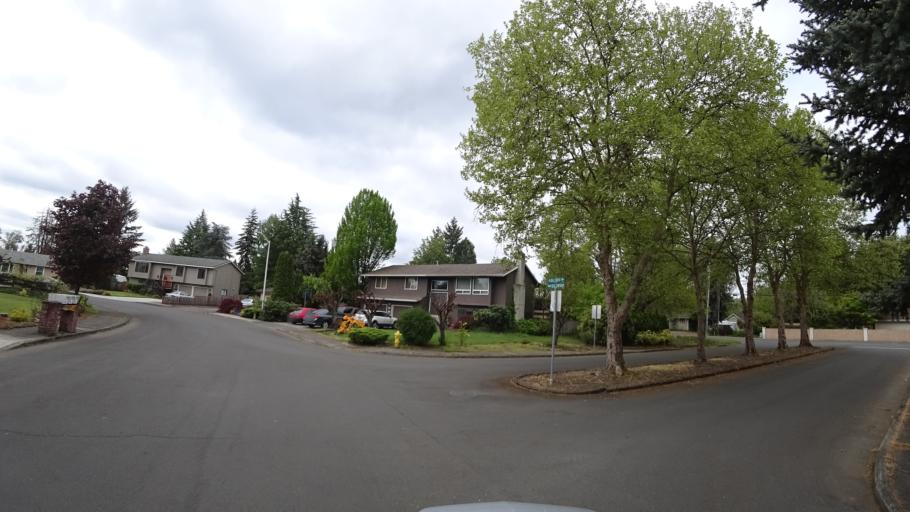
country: US
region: Oregon
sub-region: Washington County
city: Hillsboro
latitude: 45.5339
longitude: -122.9789
